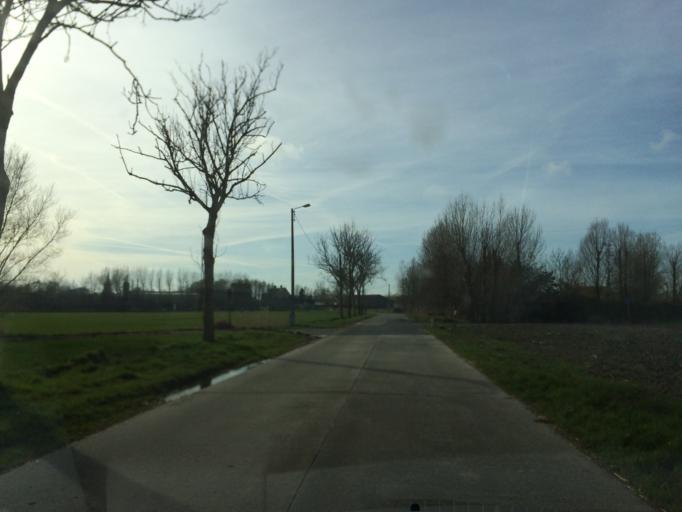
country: BE
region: Flanders
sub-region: Provincie West-Vlaanderen
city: Nieuwpoort
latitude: 51.1111
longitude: 2.7712
